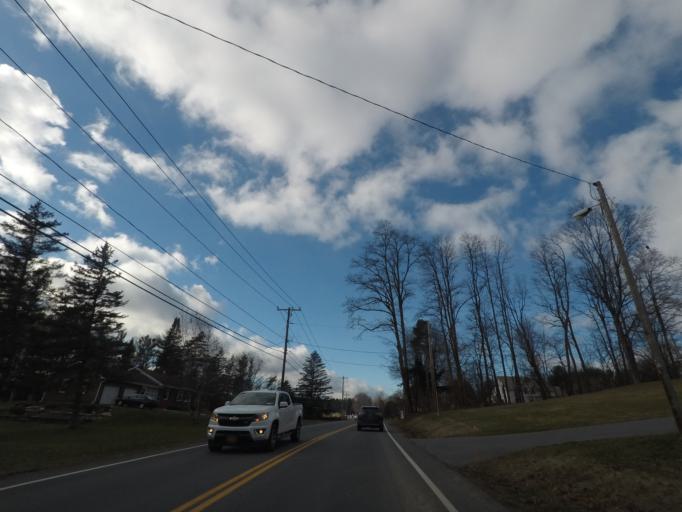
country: US
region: New York
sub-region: Schenectady County
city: East Glenville
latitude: 42.8675
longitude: -73.9172
